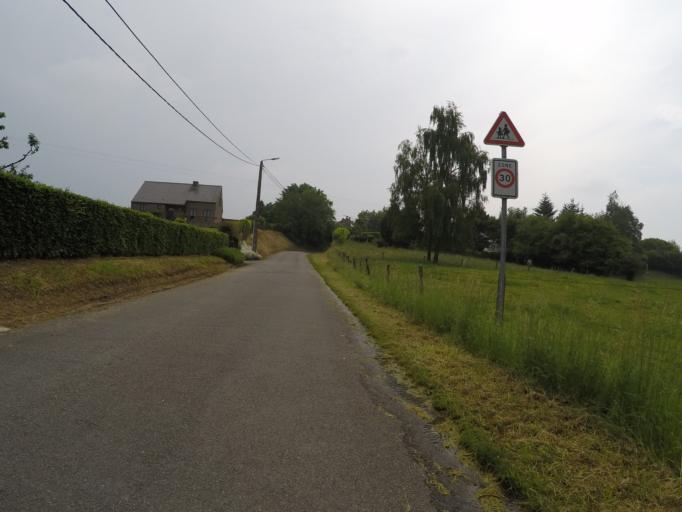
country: BE
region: Wallonia
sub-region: Province de Namur
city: Assesse
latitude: 50.3404
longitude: 4.9841
